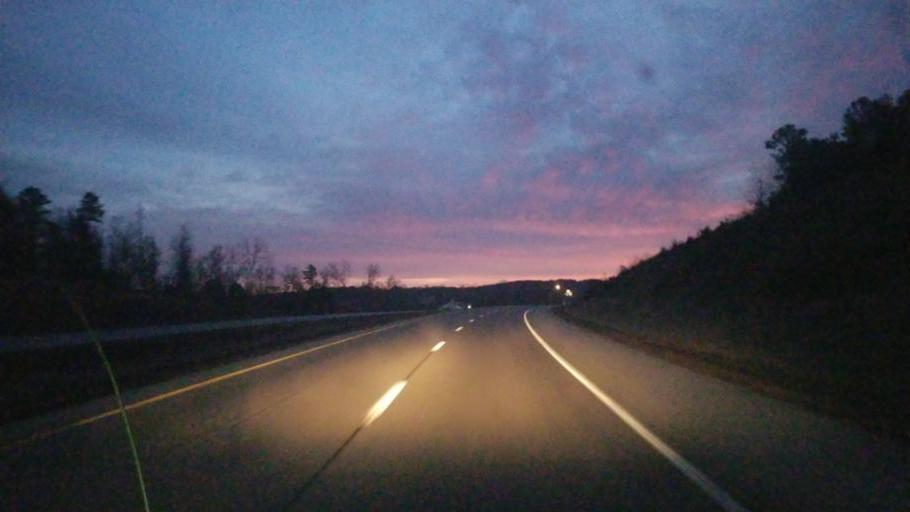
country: US
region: Missouri
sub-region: Shannon County
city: Winona
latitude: 36.9992
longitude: -91.4984
